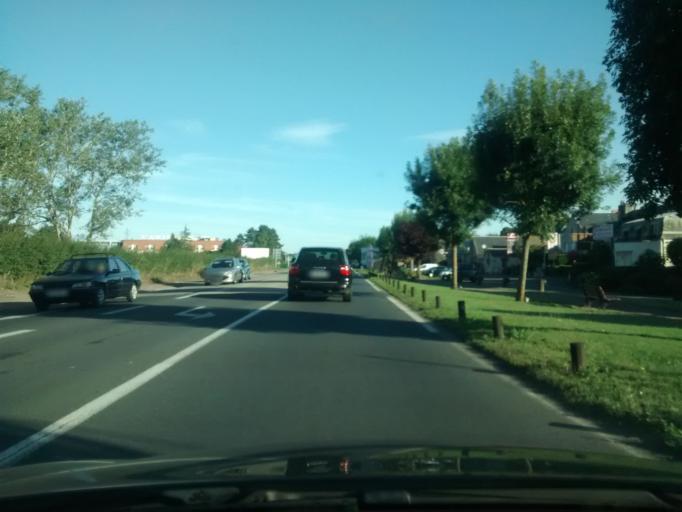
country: FR
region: Lower Normandy
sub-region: Departement du Calvados
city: Touques
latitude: 49.3403
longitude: 0.1030
